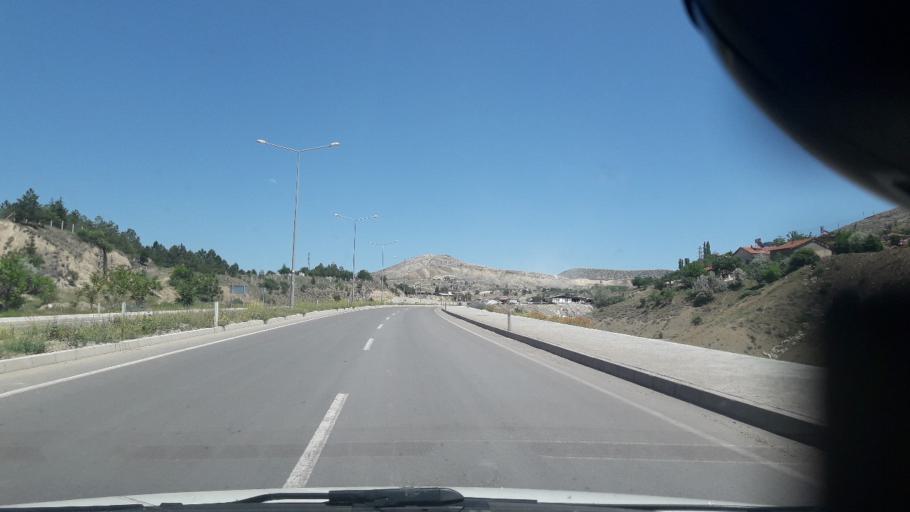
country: TR
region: Malatya
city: Hekimhan
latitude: 38.8190
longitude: 37.9350
